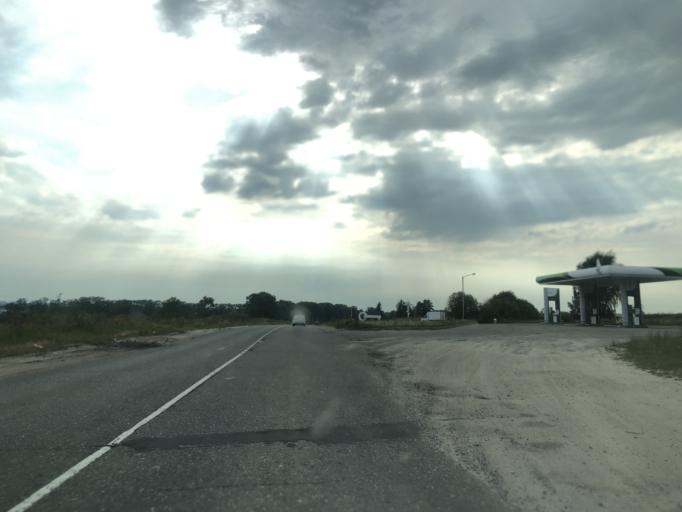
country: RU
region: Ivanovo
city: Shuya
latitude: 56.8580
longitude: 41.4394
